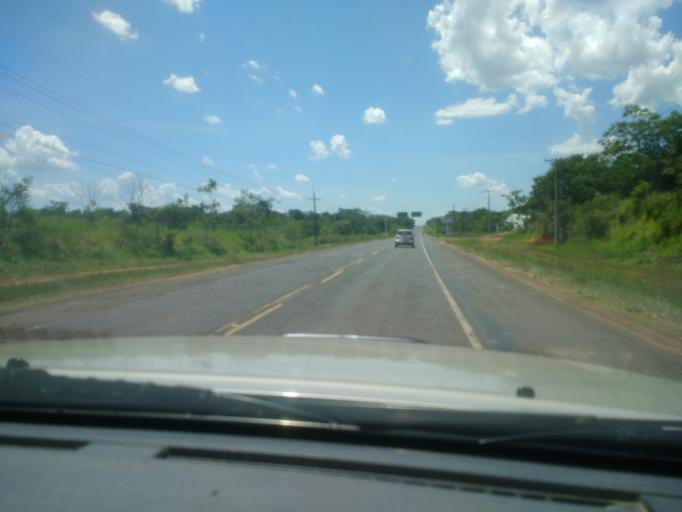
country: PY
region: San Pedro
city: Itacurubi del Rosario
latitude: -24.5240
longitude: -56.8414
